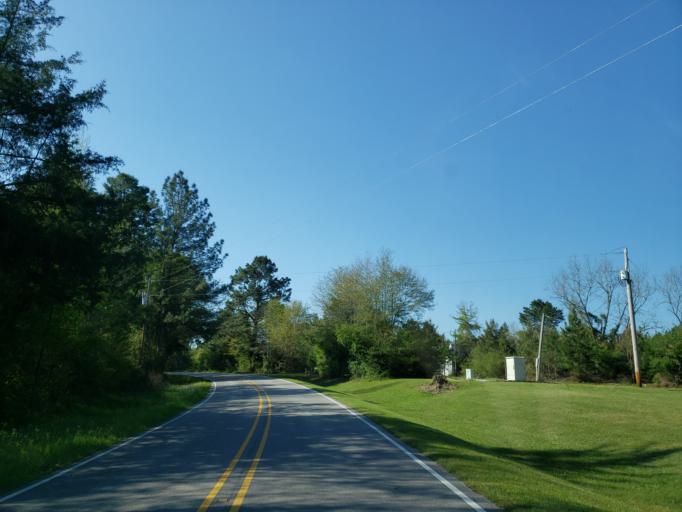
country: US
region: Mississippi
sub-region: Covington County
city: Collins
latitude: 31.6114
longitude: -89.3820
